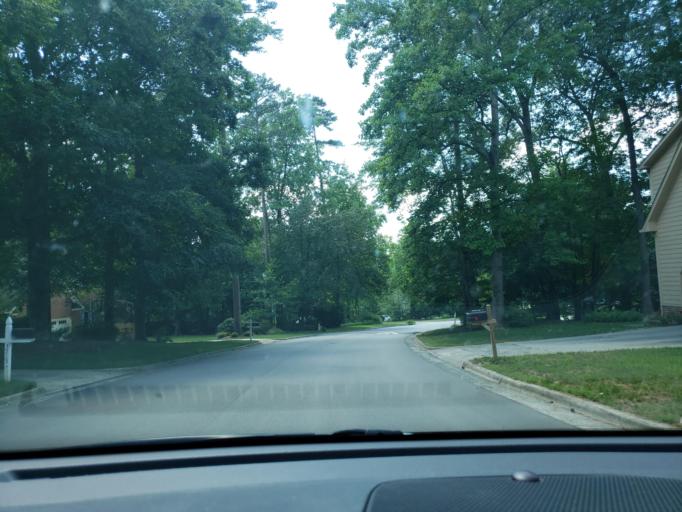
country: US
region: North Carolina
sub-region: Durham County
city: Durham
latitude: 35.9691
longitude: -78.9804
